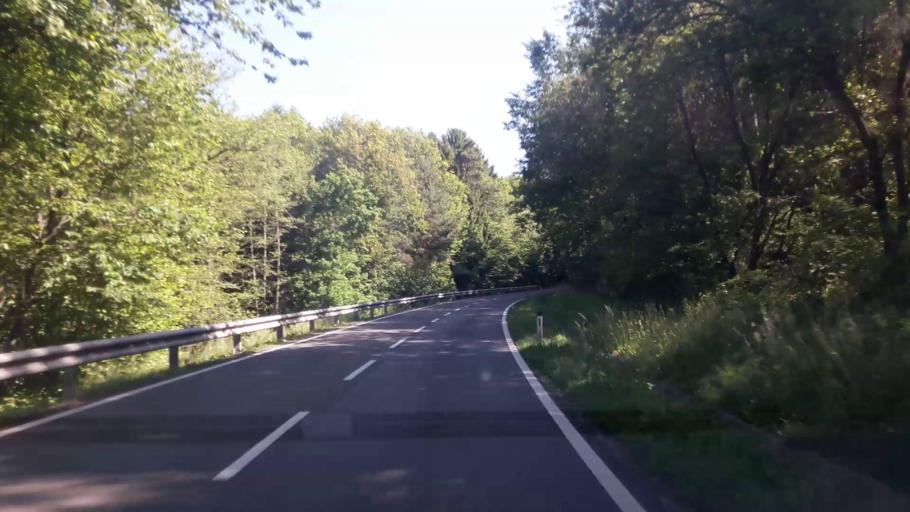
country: AT
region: Styria
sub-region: Politischer Bezirk Hartberg-Fuerstenfeld
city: Neudau
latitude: 47.1563
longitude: 16.1194
